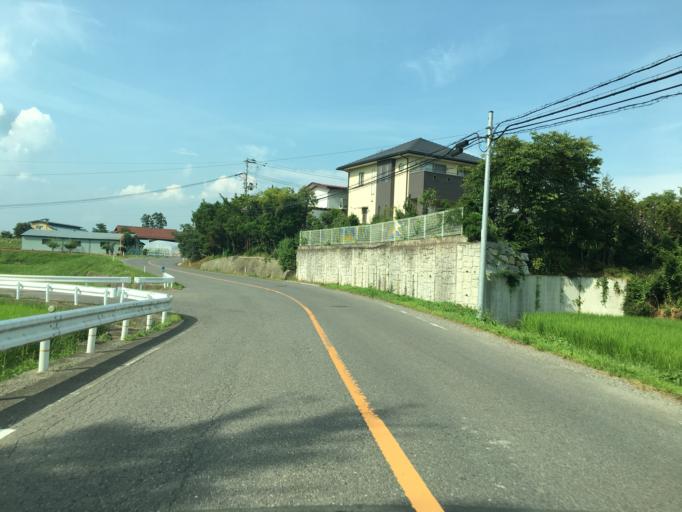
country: JP
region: Fukushima
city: Koriyama
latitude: 37.3458
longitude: 140.4121
